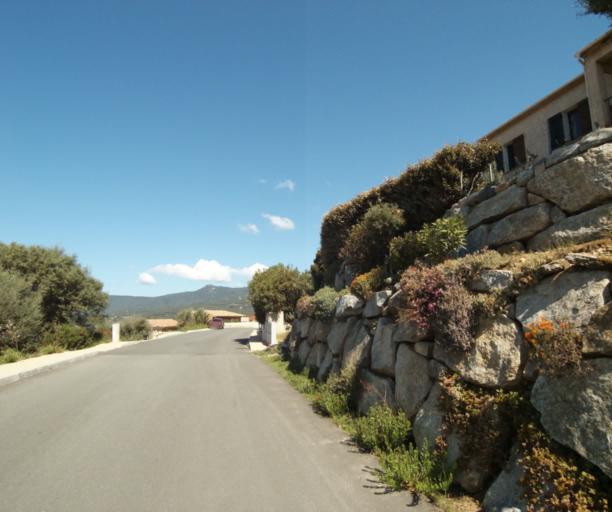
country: FR
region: Corsica
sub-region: Departement de la Corse-du-Sud
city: Propriano
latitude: 41.6756
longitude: 8.9110
